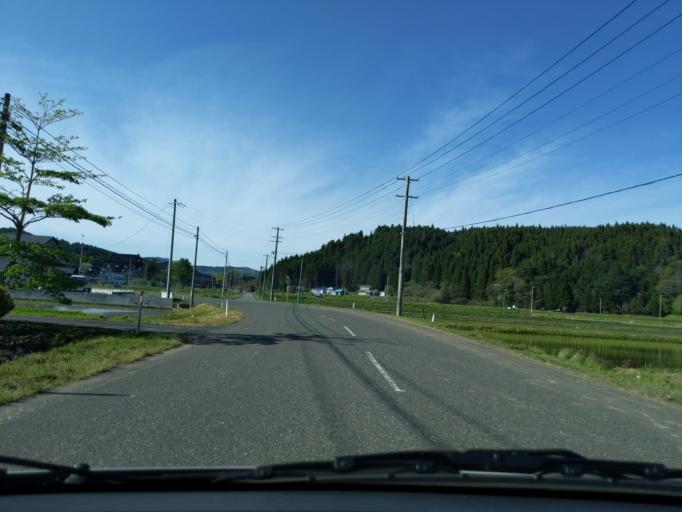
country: JP
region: Iwate
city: Ichinoseki
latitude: 38.8399
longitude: 140.9090
